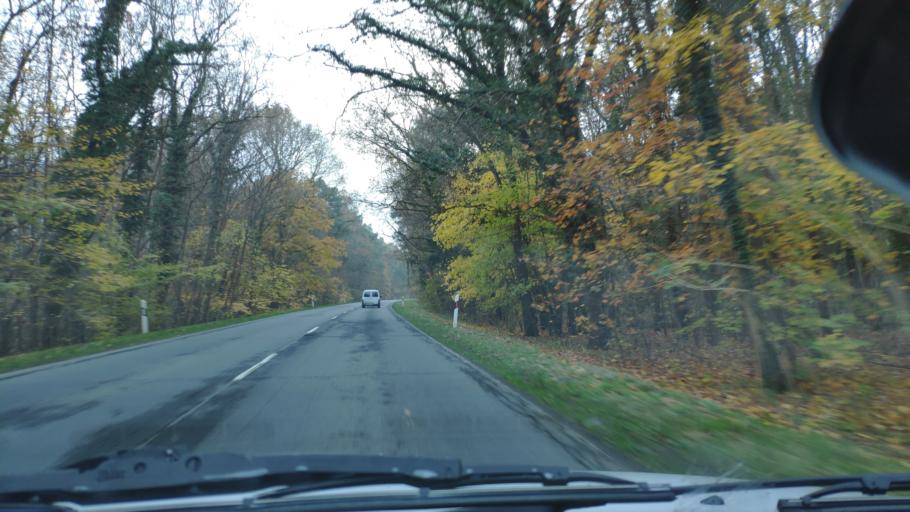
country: HU
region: Zala
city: Zalakomar
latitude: 46.5439
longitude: 17.2489
